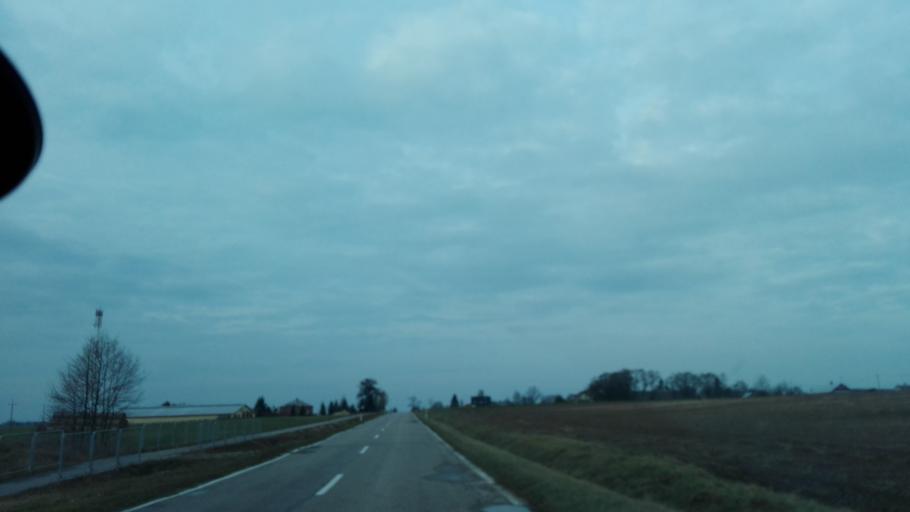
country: PL
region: Lublin Voivodeship
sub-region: Powiat bialski
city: Slawatycze
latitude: 51.6660
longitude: 23.5156
